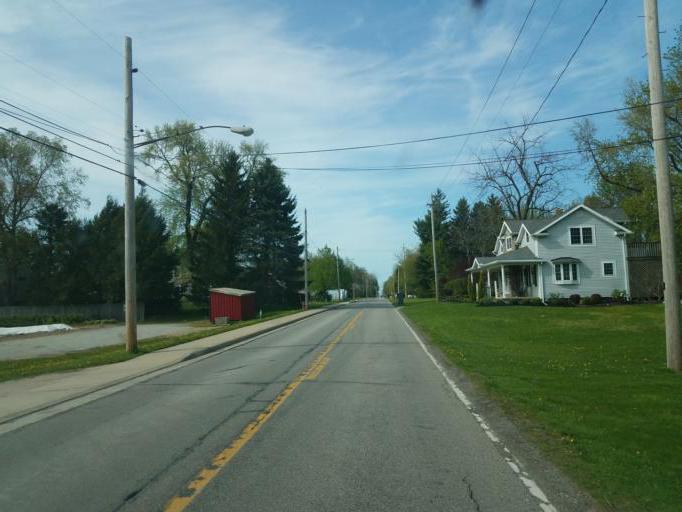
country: US
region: Ohio
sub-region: Lake County
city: North Madison
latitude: 41.8052
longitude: -81.1047
